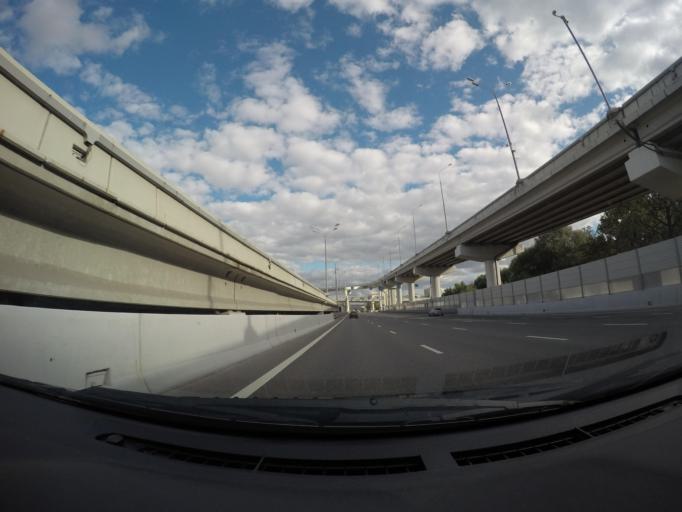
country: RU
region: Moscow
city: Novokhovrino
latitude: 55.8685
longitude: 37.5091
